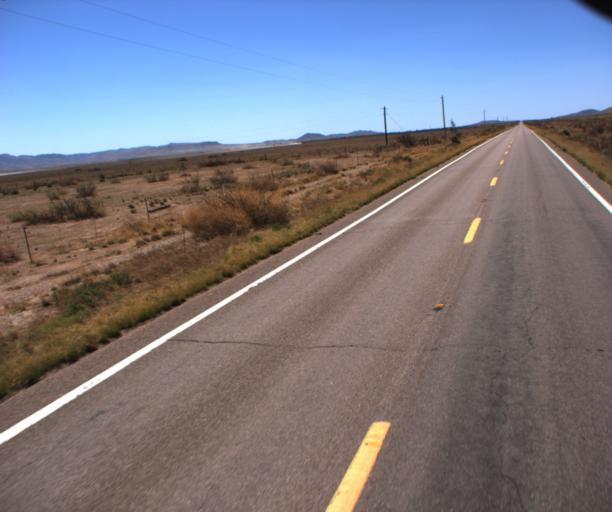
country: US
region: Arizona
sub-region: Cochise County
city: Douglas
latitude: 31.7278
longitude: -109.1069
